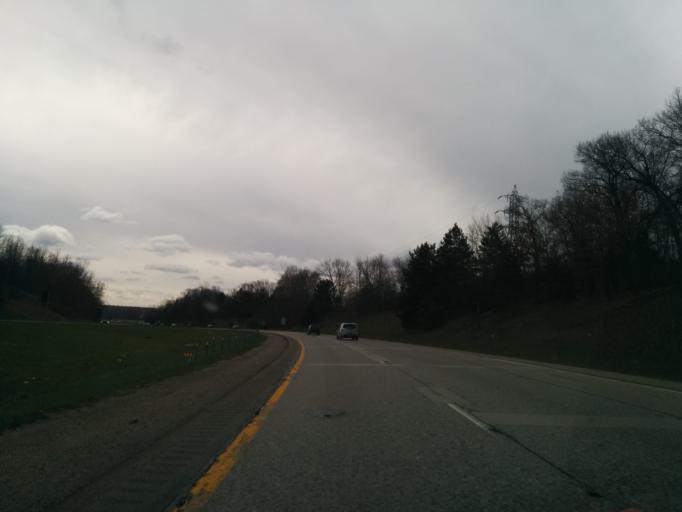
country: US
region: Michigan
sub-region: Kent County
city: Grand Rapids
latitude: 42.9621
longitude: -85.7088
